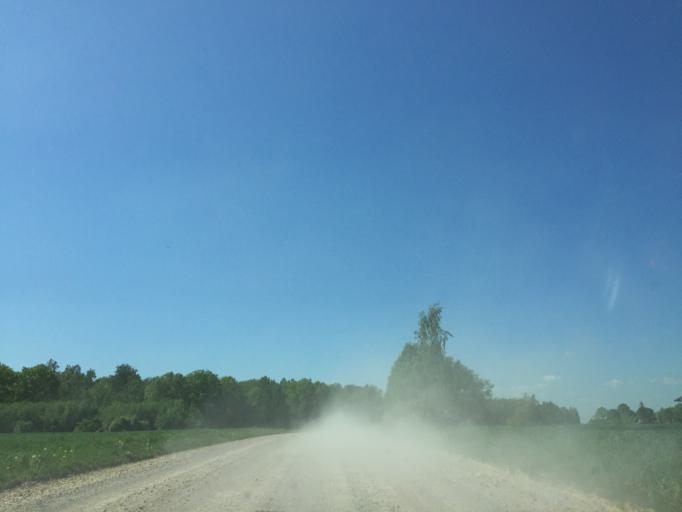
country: LV
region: Bauskas Rajons
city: Bauska
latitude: 56.4787
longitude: 24.1318
